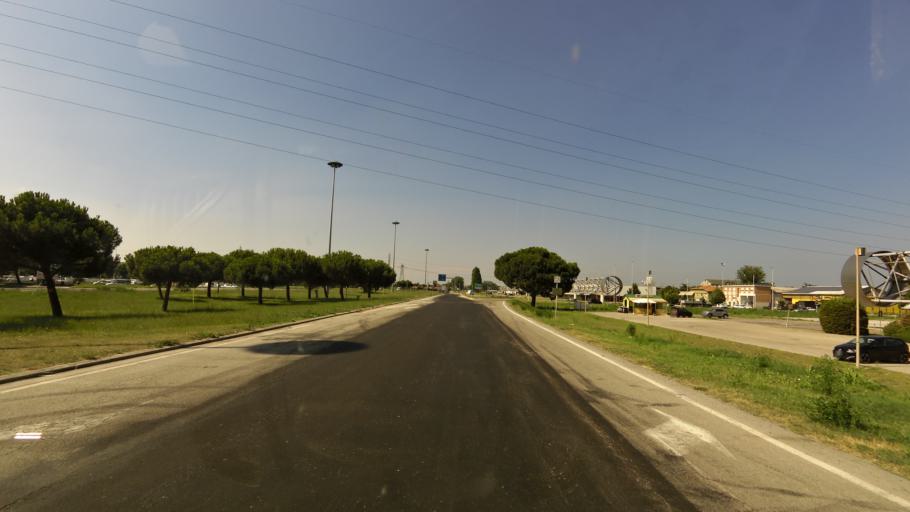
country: IT
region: Emilia-Romagna
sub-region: Provincia di Ravenna
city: Ravenna
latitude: 44.4474
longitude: 12.2102
